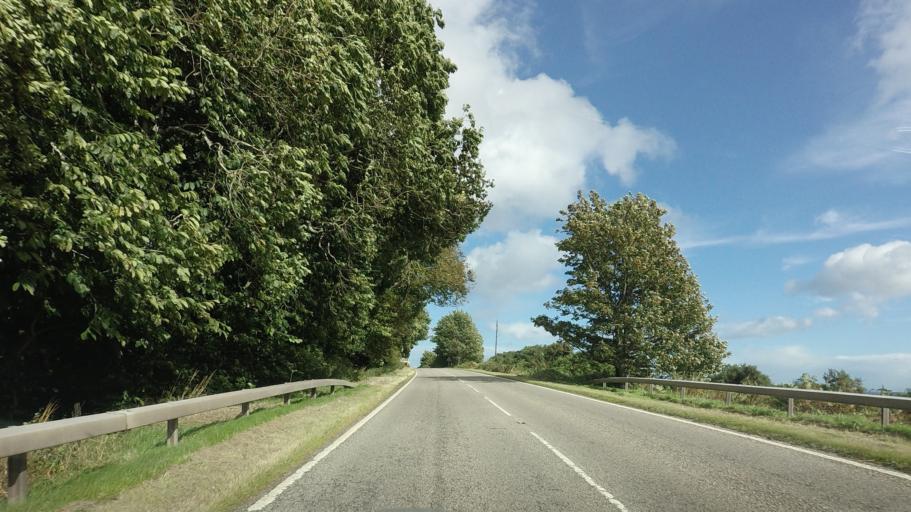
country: GB
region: Scotland
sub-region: Highland
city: Brora
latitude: 58.0887
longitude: -3.7167
